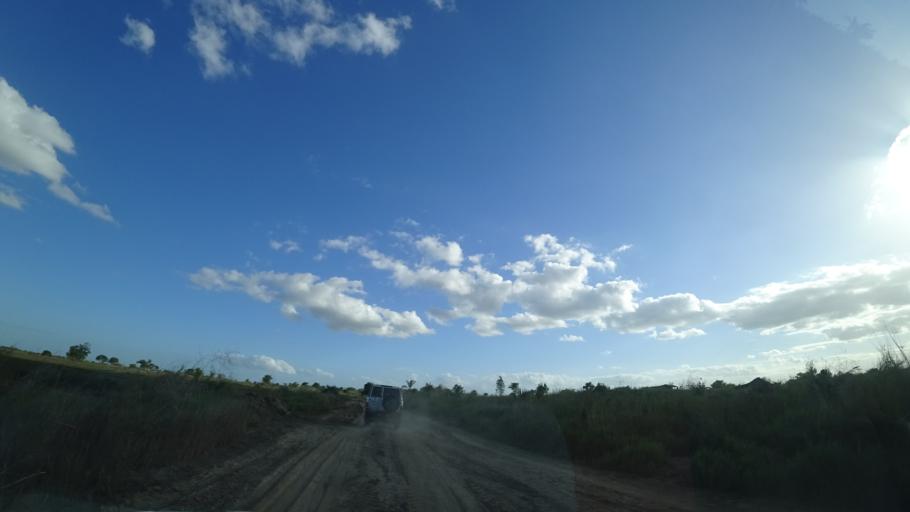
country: MZ
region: Sofala
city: Dondo
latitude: -19.4212
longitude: 34.5637
